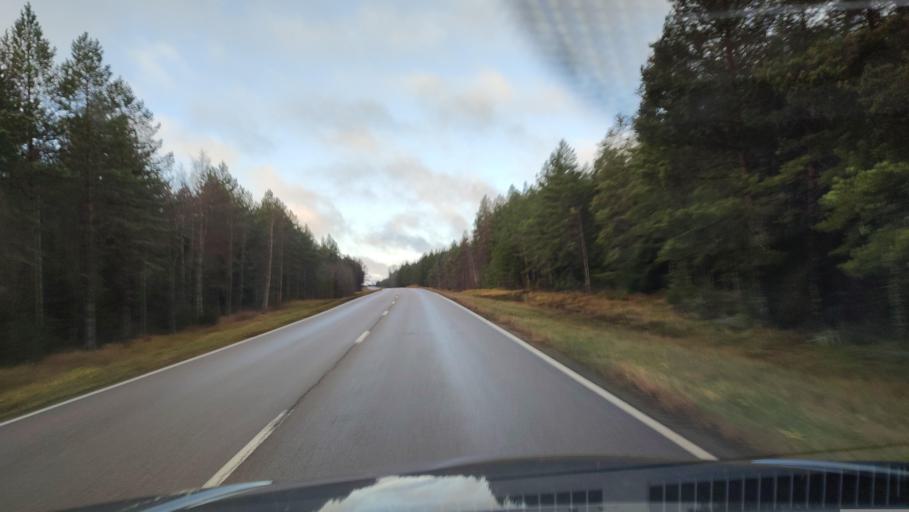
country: FI
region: Ostrobothnia
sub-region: Sydosterbotten
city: Kristinestad
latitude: 62.3018
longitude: 21.4137
